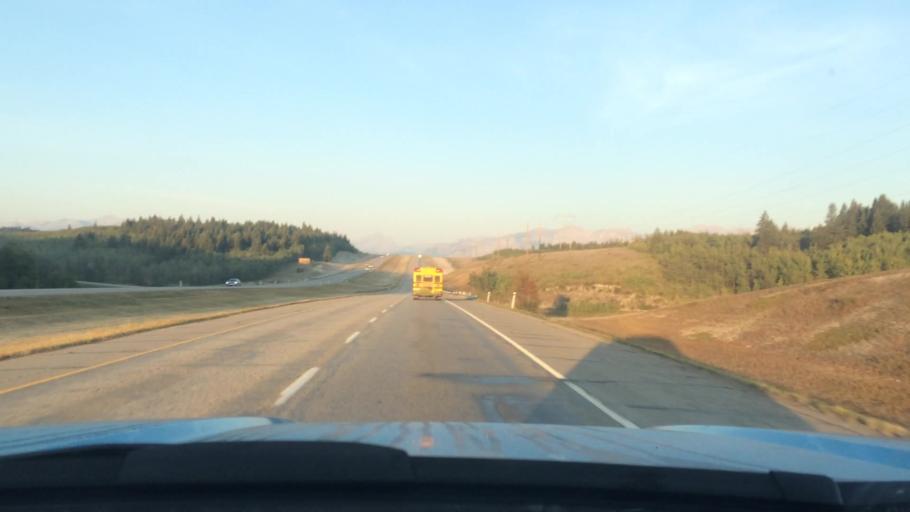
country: CA
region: Alberta
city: Cochrane
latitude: 51.1444
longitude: -114.8716
